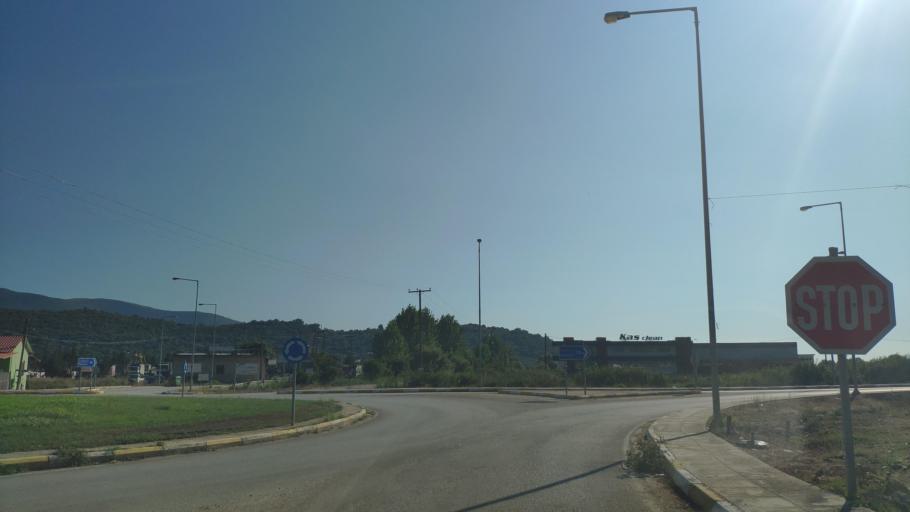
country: GR
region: Epirus
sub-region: Nomos Prevezis
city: Kanalaki
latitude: 39.2418
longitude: 20.5873
